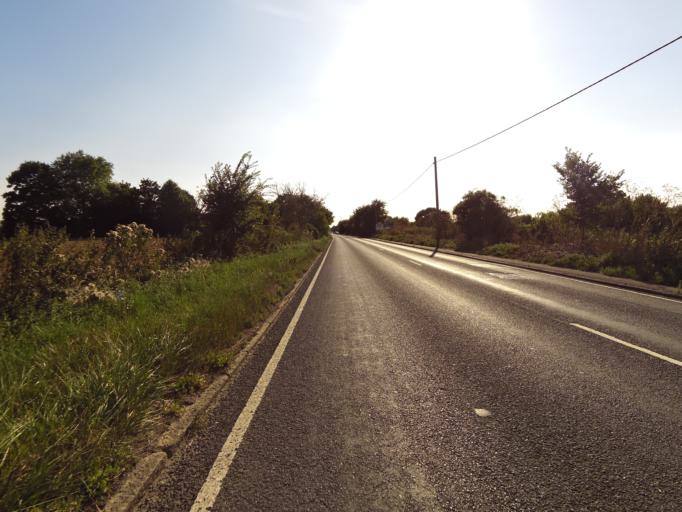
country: GB
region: England
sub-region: Essex
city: Hatfield Peverel
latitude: 51.7679
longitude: 0.5585
